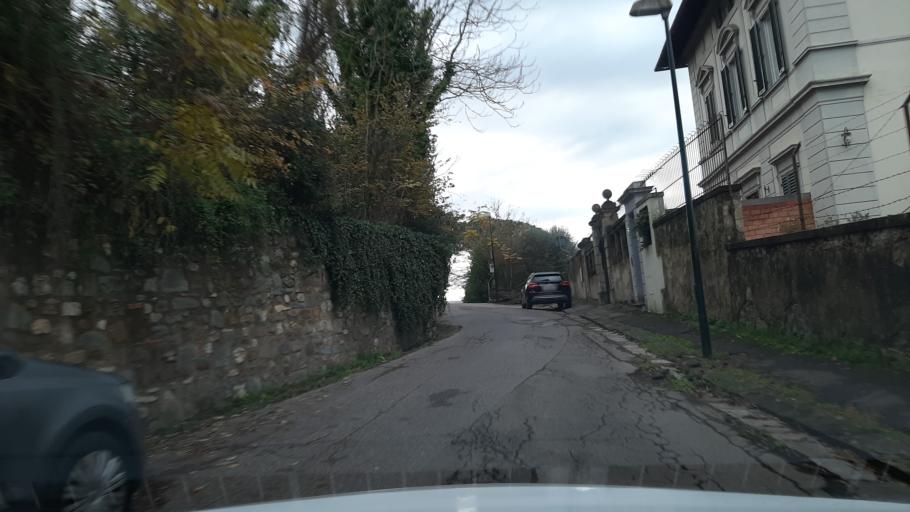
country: IT
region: Tuscany
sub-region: Province of Florence
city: Fiesole
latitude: 43.7836
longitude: 11.2967
